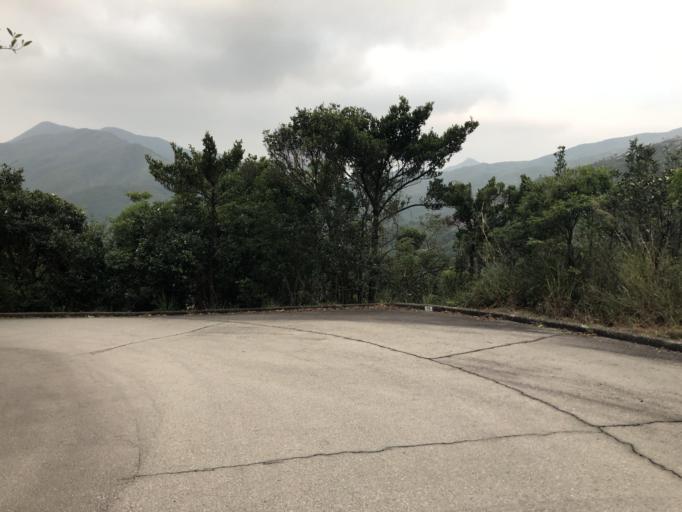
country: HK
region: Wanchai
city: Wan Chai
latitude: 22.2637
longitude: 114.2137
